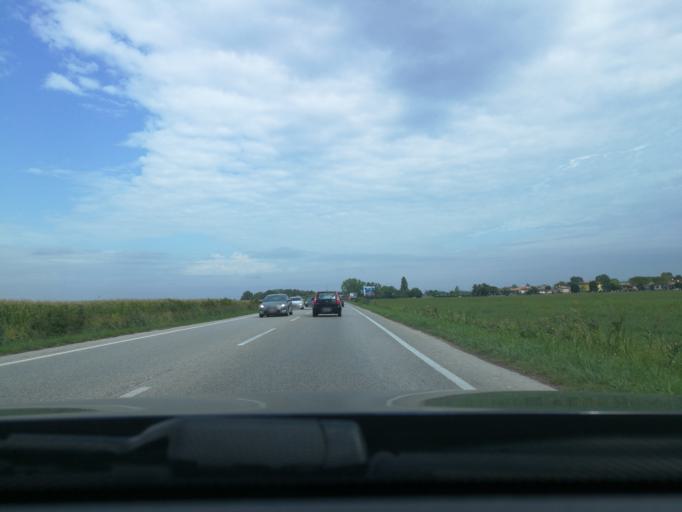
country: IT
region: Veneto
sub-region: Provincia di Venezia
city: Bibione
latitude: 45.6659
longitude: 13.0571
